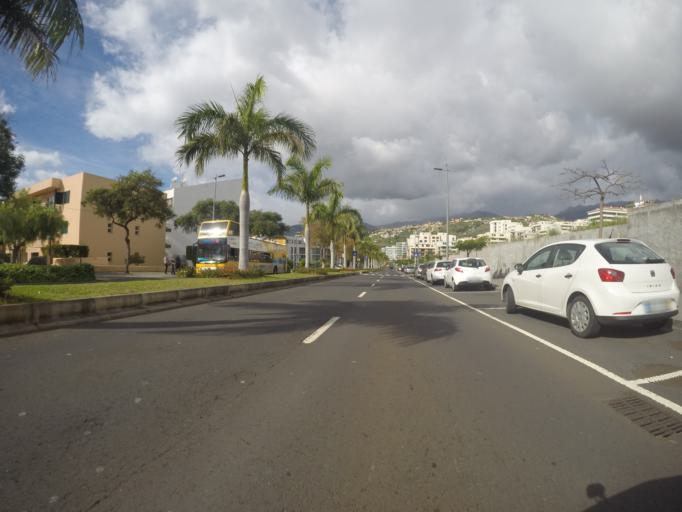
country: PT
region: Madeira
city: Camara de Lobos
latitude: 32.6375
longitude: -16.9452
